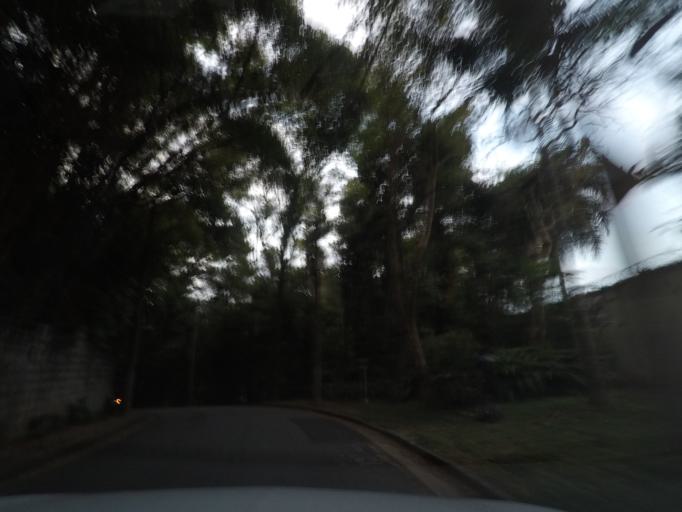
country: BR
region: Sao Paulo
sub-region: Taboao Da Serra
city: Taboao da Serra
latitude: -23.6133
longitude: -46.7113
